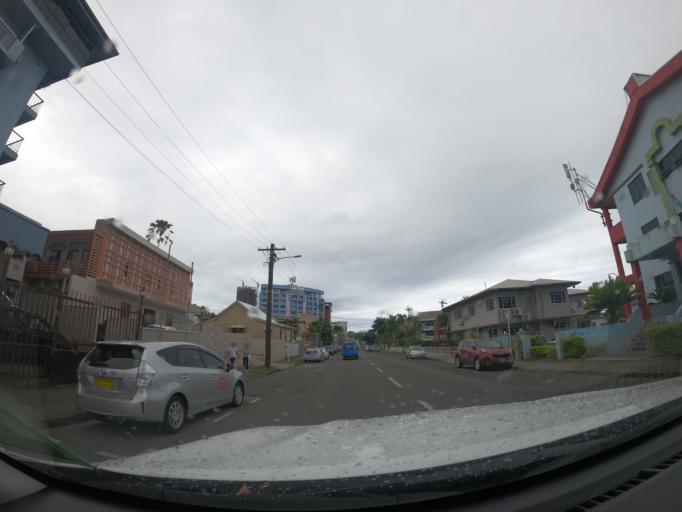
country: FJ
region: Central
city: Suva
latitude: -18.1428
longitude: 178.4254
